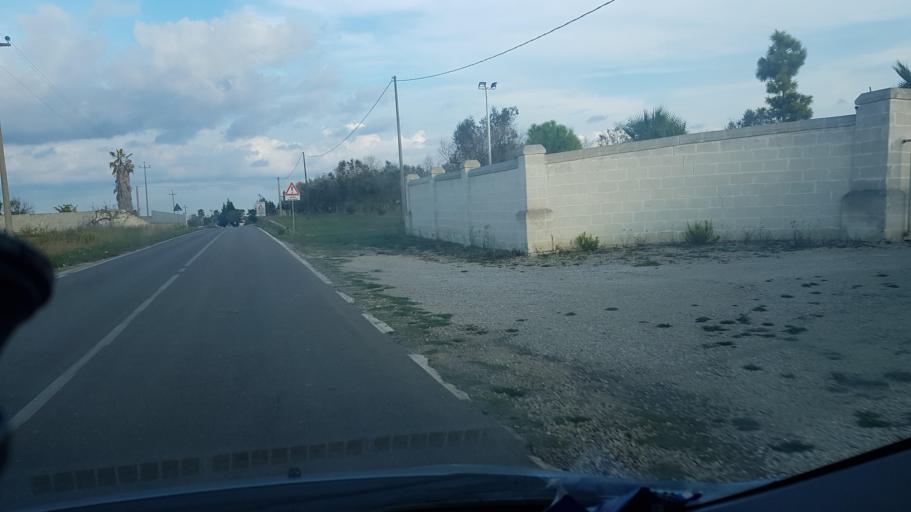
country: IT
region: Apulia
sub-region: Provincia di Lecce
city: Carmiano
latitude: 40.3453
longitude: 18.0210
